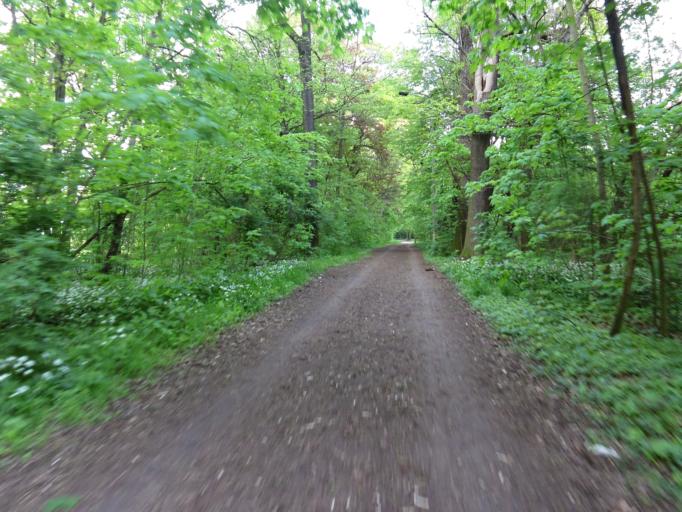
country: DE
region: Saxony
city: Leipzig
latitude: 51.3105
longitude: 12.3357
